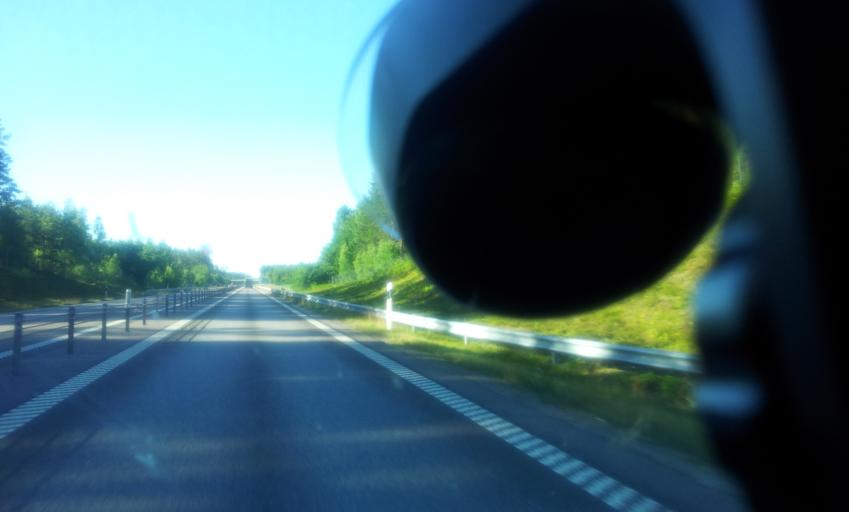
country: SE
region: Kalmar
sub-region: Torsas Kommun
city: Torsas
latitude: 56.5210
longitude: 16.0850
